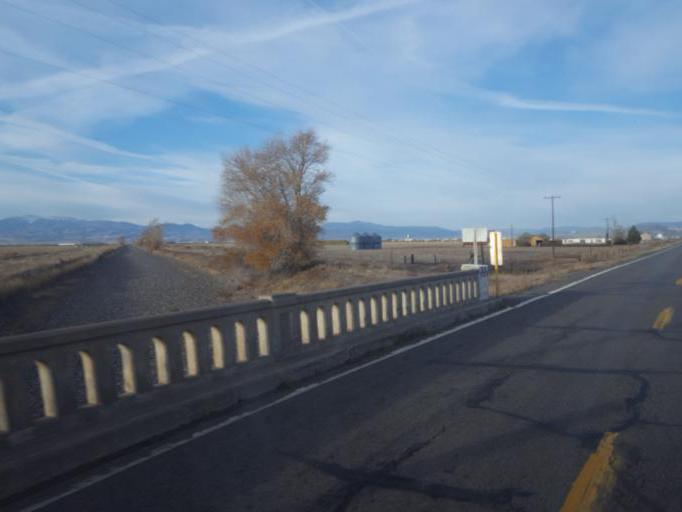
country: US
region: Colorado
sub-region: Saguache County
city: Center
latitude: 37.7481
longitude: -106.1574
